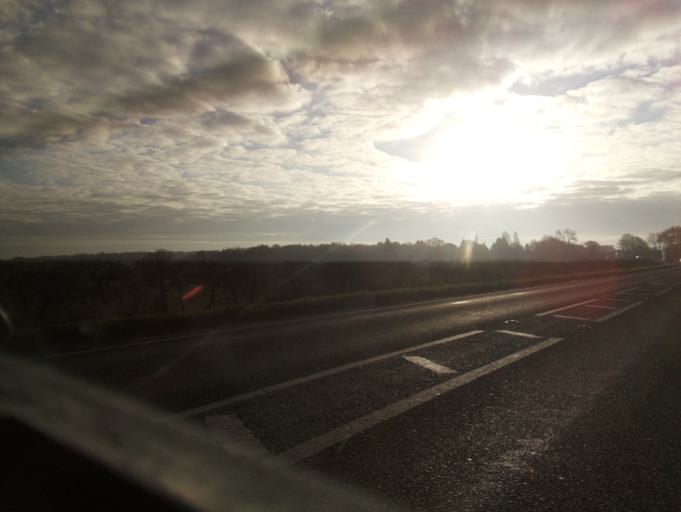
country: GB
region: England
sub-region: City and Borough of Birmingham
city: Sutton Coldfield
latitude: 52.5834
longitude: -1.7785
